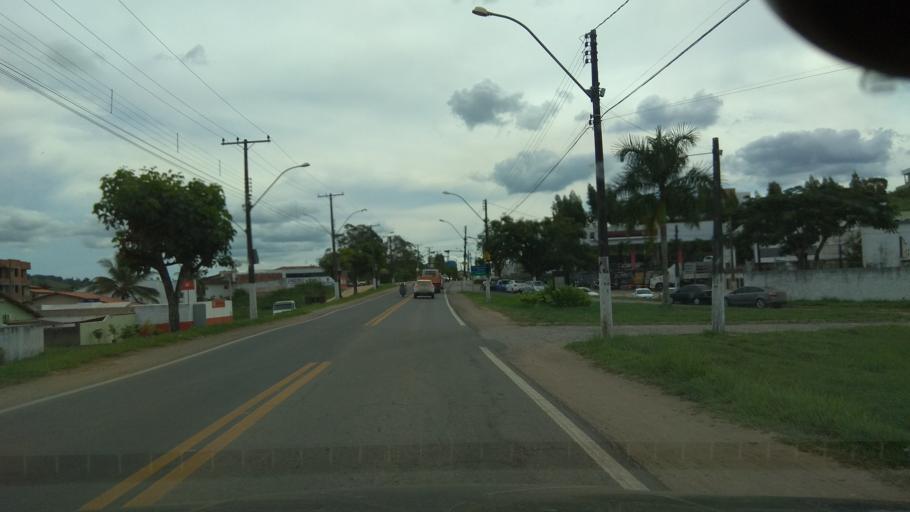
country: BR
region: Bahia
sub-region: Ipiau
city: Ipiau
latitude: -14.1414
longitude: -39.7257
